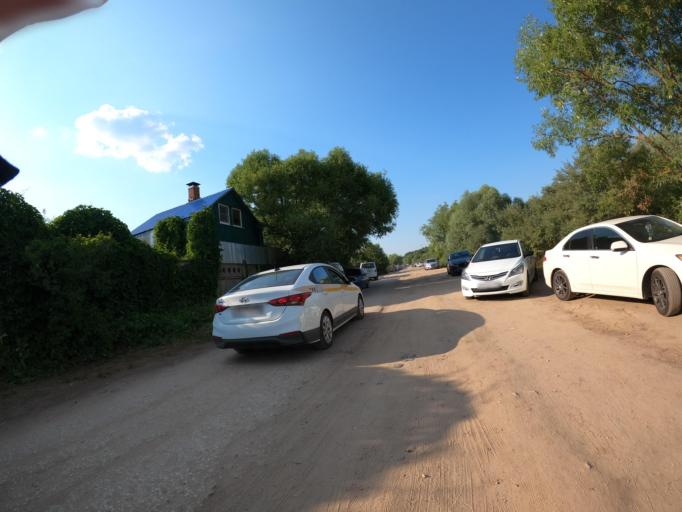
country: RU
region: Moskovskaya
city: Protvino
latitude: 54.8606
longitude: 37.1895
